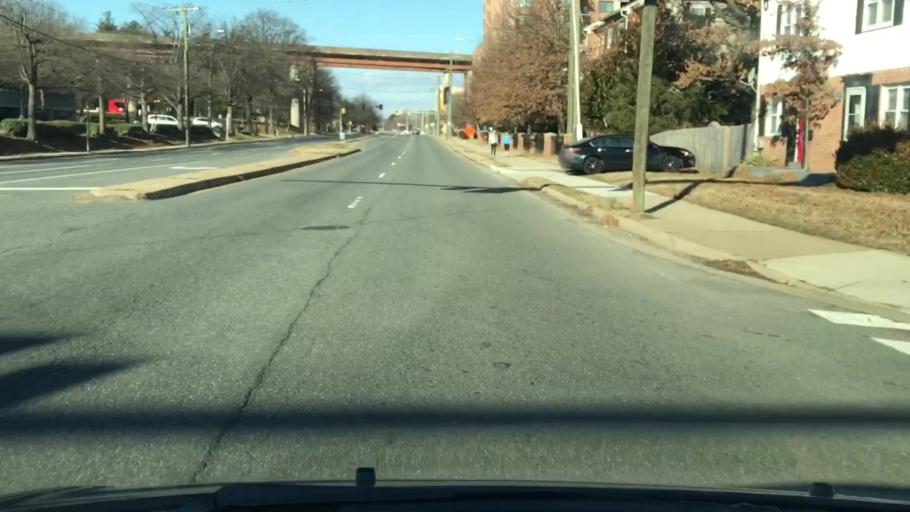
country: US
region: Virginia
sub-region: Fairfax County
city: Huntington
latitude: 38.7952
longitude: -77.0729
